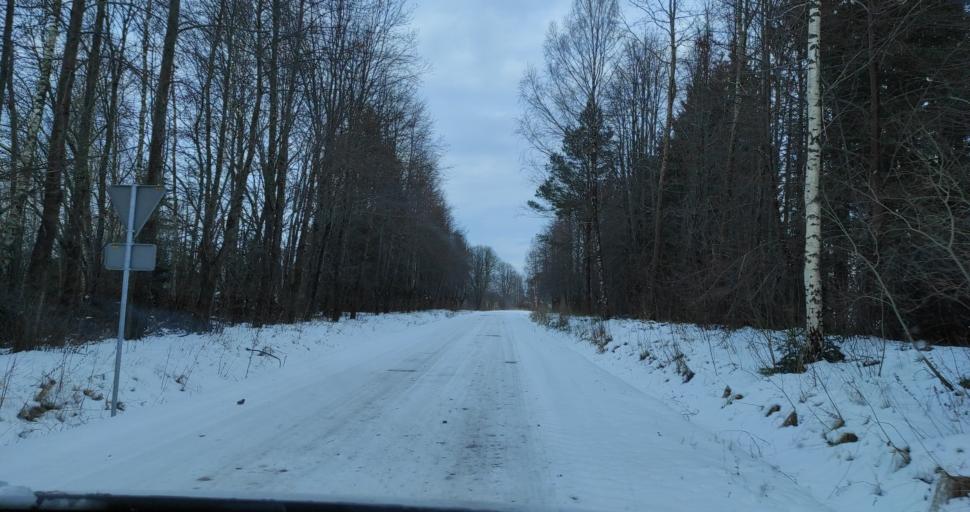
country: LV
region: Kuldigas Rajons
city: Kuldiga
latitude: 56.9397
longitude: 22.0276
